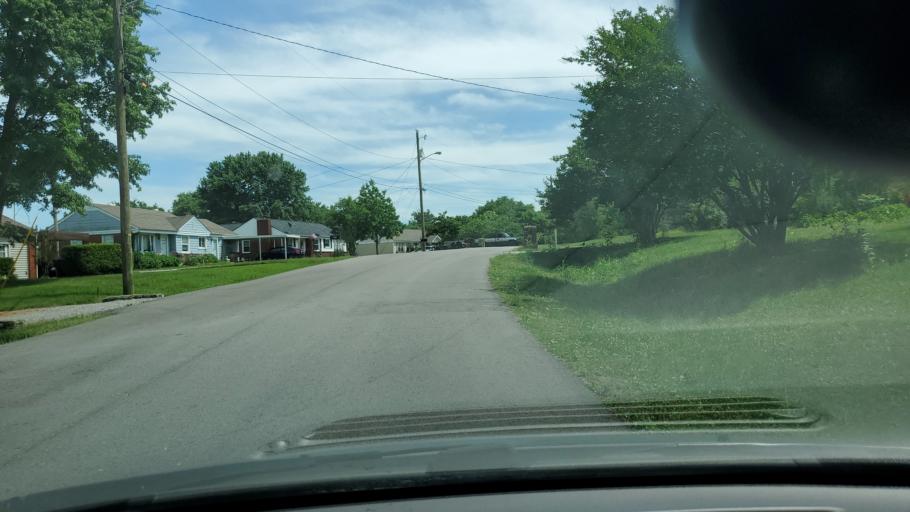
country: US
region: Tennessee
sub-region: Davidson County
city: Nashville
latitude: 36.2355
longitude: -86.7305
